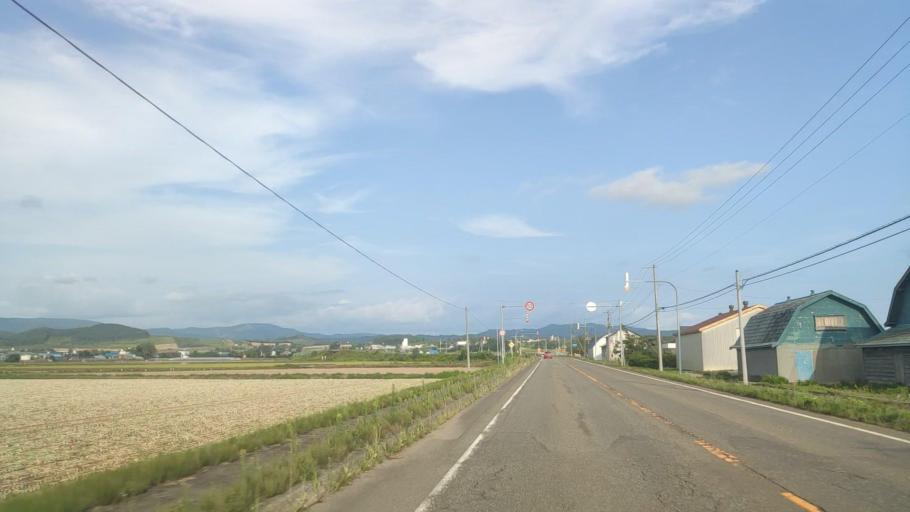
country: JP
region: Hokkaido
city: Iwamizawa
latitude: 43.0275
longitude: 141.8199
